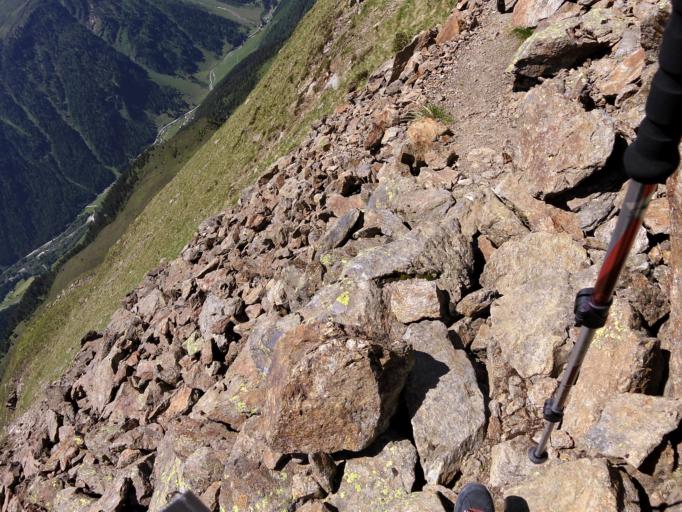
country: AT
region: Tyrol
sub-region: Politischer Bezirk Innsbruck Land
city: Neustift im Stubaital
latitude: 47.1340
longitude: 11.2393
